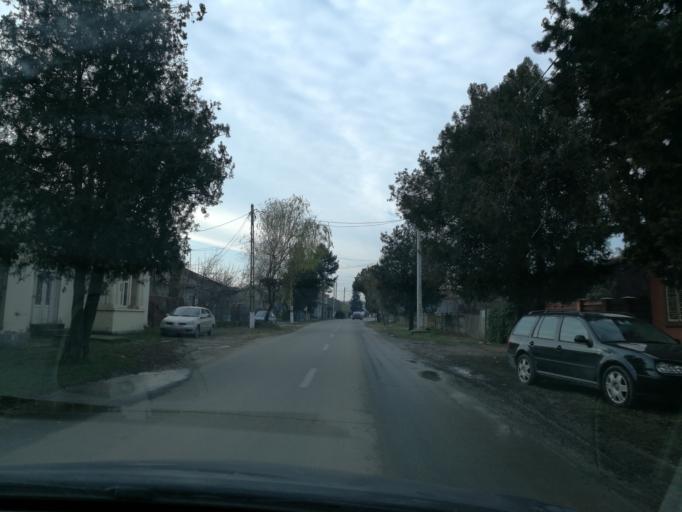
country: RO
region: Ialomita
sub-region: Comuna Fierbinti-Targ
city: Fierbintii de Jos
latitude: 44.6845
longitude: 26.3858
